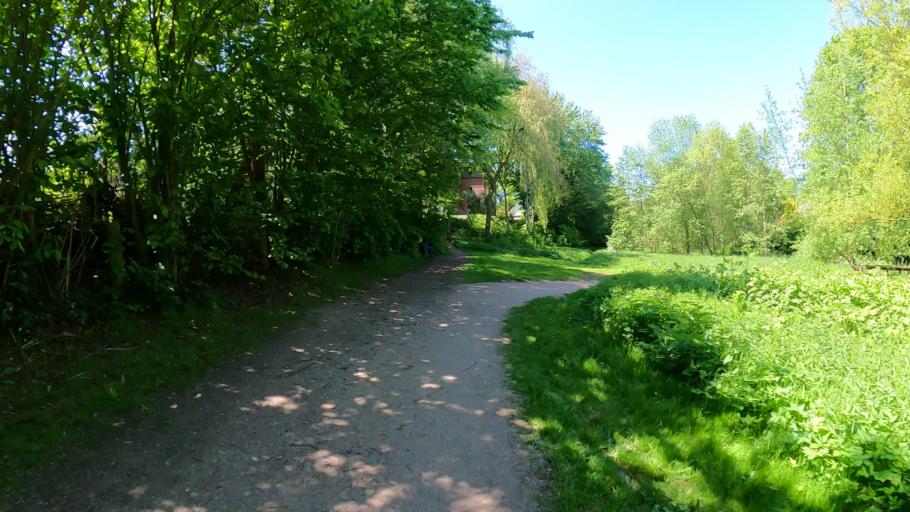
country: DE
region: Hamburg
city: Harburg
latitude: 53.4515
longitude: 9.9587
